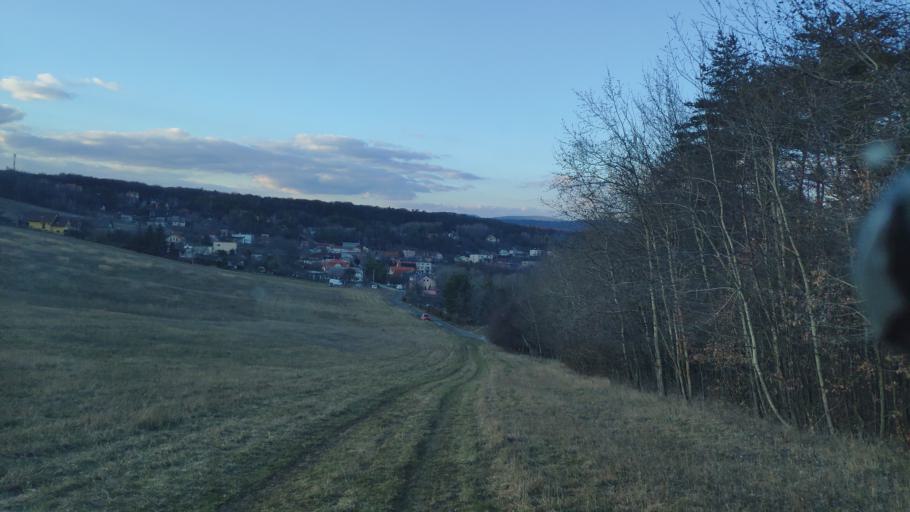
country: SK
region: Kosicky
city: Kosice
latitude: 48.7005
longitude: 21.1809
